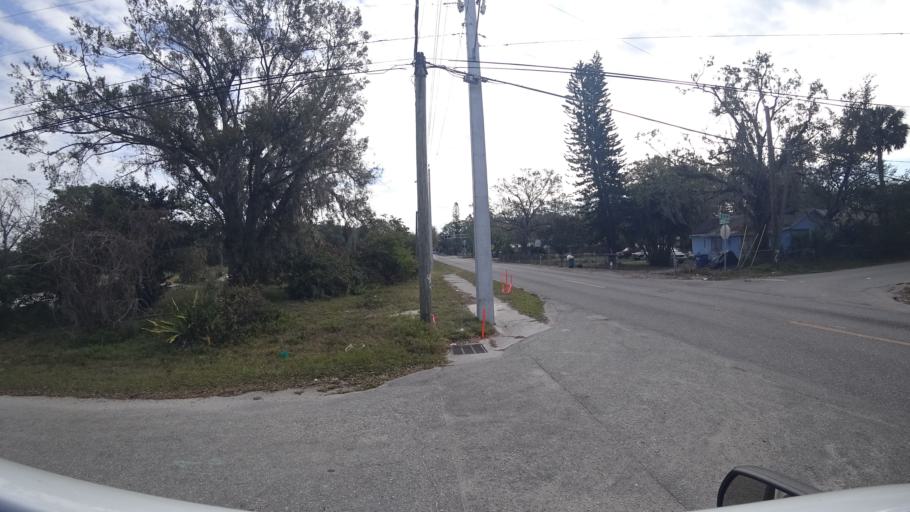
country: US
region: Florida
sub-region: Manatee County
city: West Samoset
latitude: 27.4734
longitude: -82.5503
